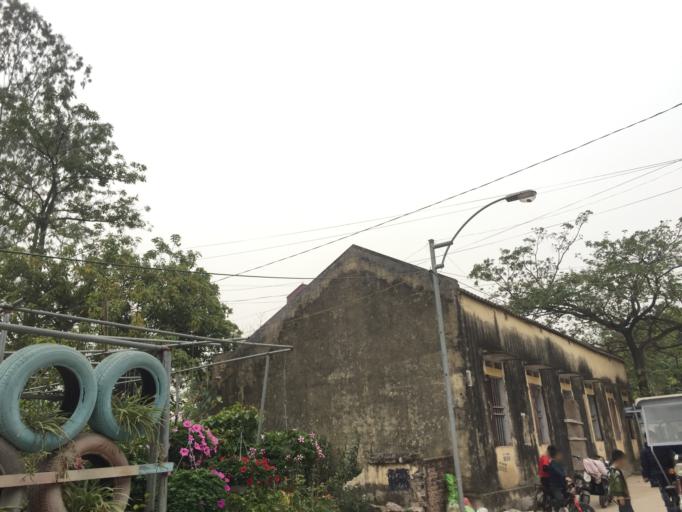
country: VN
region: Hung Yen
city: Van Giang
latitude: 20.9700
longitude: 105.9205
